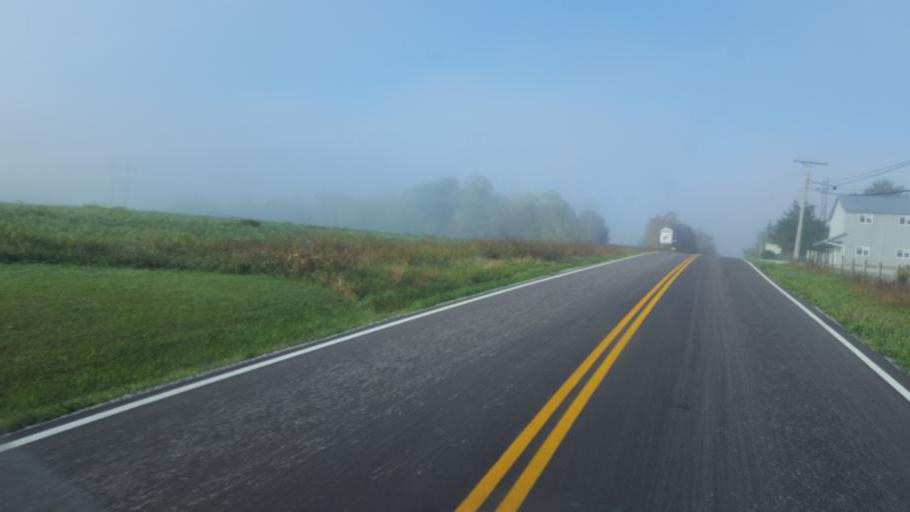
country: US
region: Kentucky
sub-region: Fleming County
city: Flemingsburg
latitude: 38.4823
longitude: -83.6429
